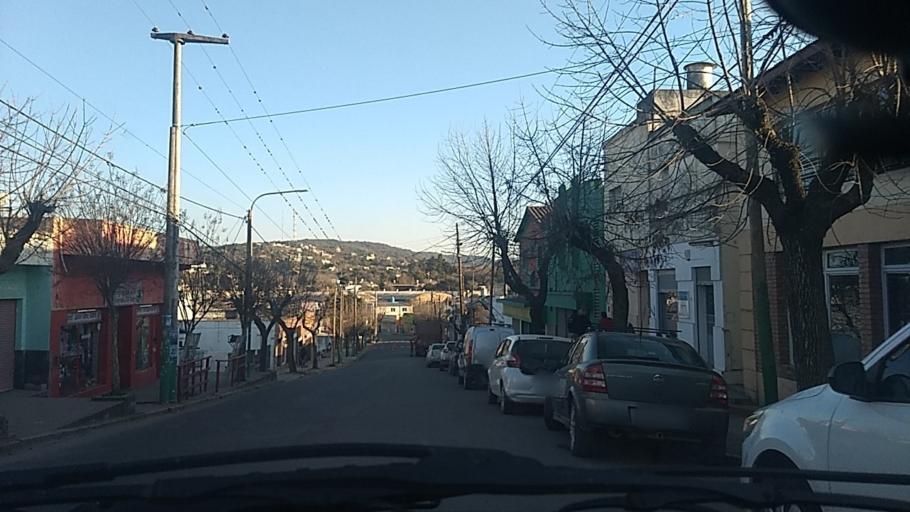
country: AR
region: Cordoba
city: Salsipuedes
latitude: -31.1384
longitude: -64.2920
